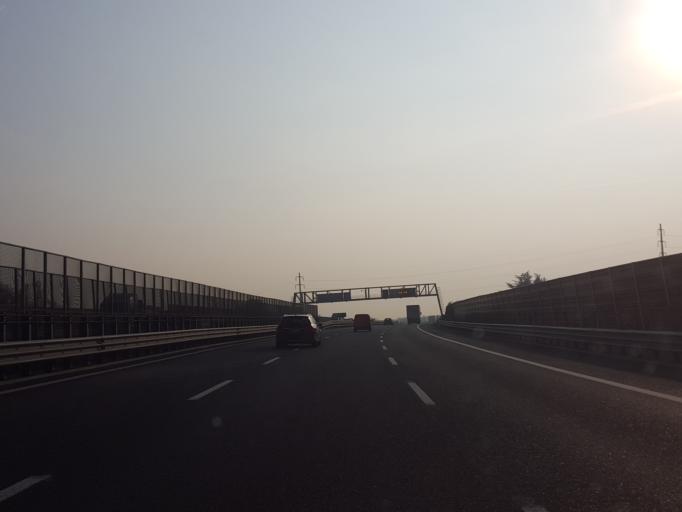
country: IT
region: Veneto
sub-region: Provincia di Venezia
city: Maerne
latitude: 45.5308
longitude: 12.1413
